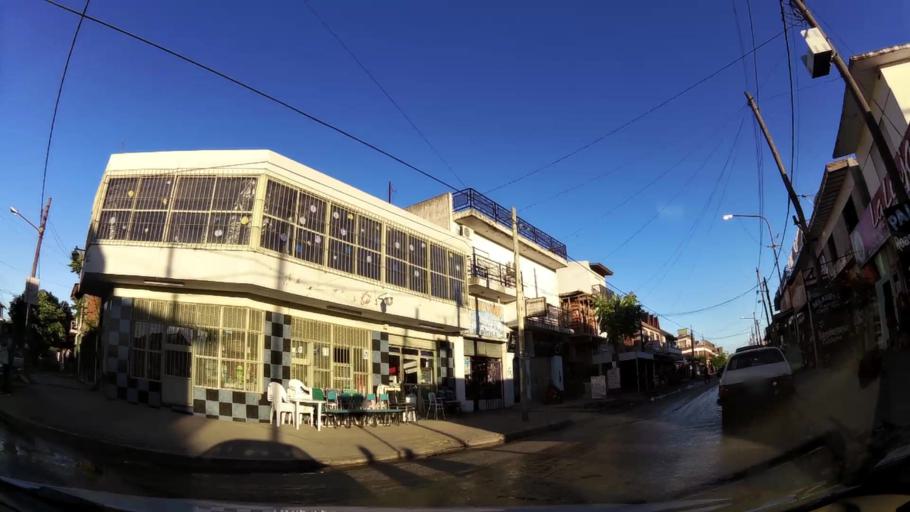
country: AR
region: Buenos Aires
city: San Justo
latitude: -34.7283
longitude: -58.6138
